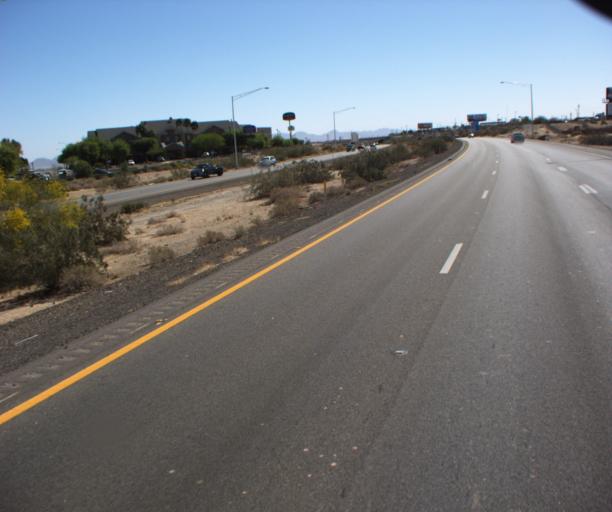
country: US
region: Arizona
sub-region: Yuma County
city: Yuma
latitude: 32.6950
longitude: -114.6050
